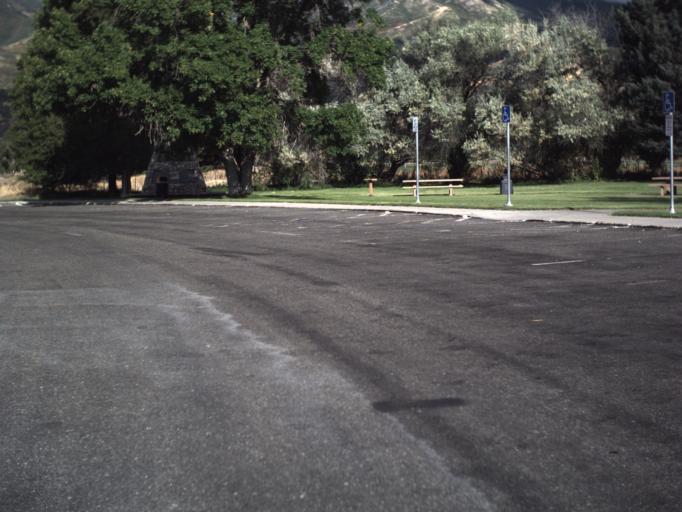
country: US
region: Utah
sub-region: Morgan County
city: Mountain Green
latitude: 41.1381
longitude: -111.7966
